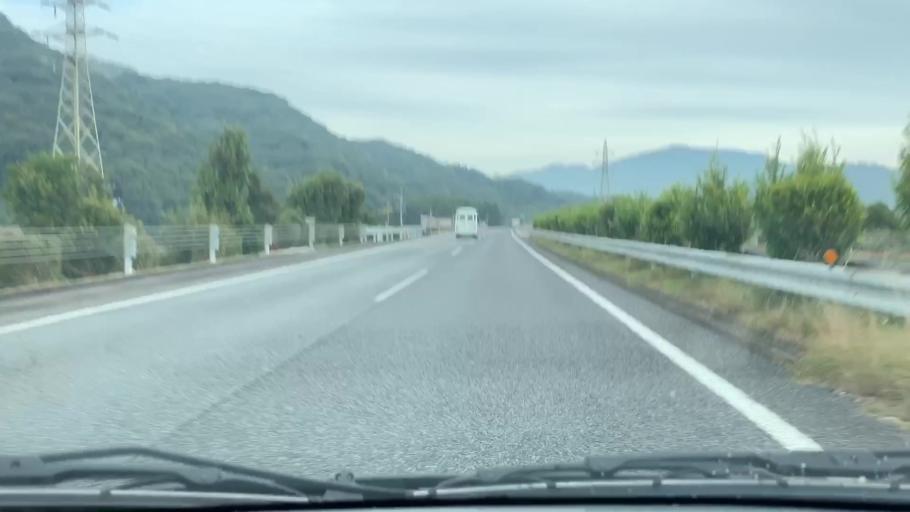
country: JP
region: Saga Prefecture
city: Takeocho-takeo
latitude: 33.2568
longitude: 130.0802
